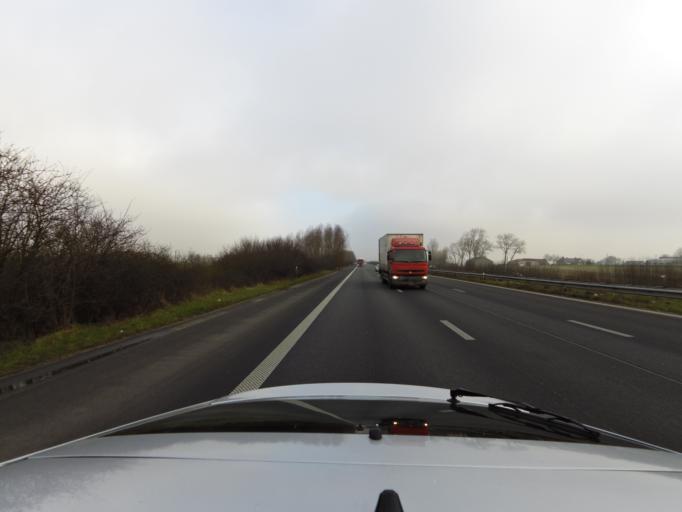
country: BE
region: Flanders
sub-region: Provincie West-Vlaanderen
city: Ledegem
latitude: 50.8646
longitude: 3.1710
